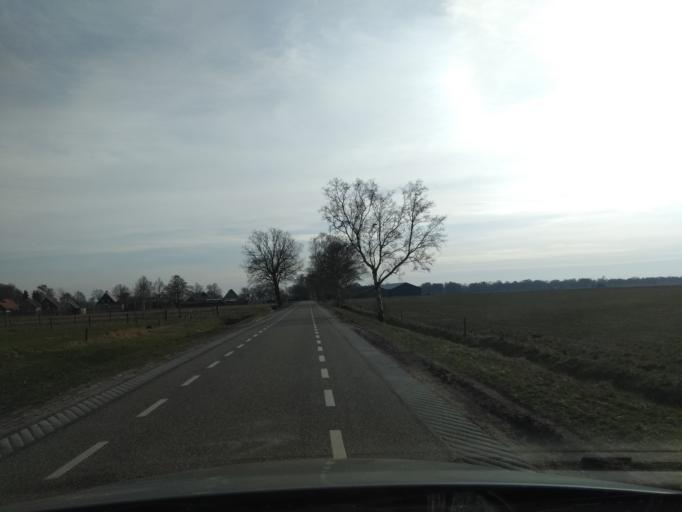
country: NL
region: Overijssel
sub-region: Gemeente Twenterand
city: Westerhaar-Vriezenveensewijk
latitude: 52.4320
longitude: 6.6568
